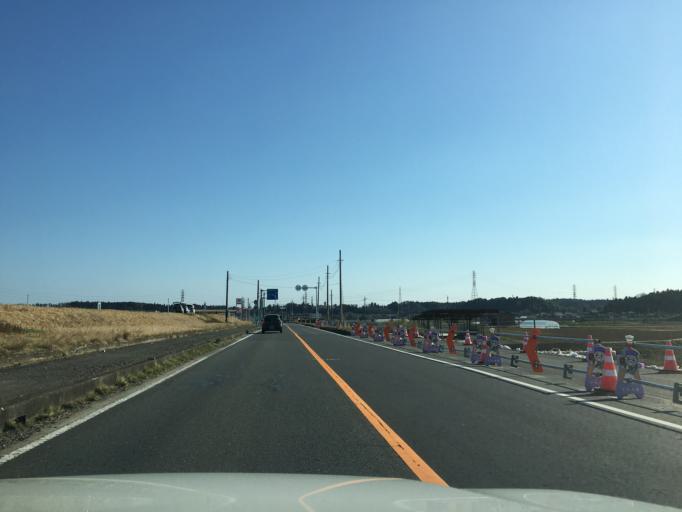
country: JP
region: Ibaraki
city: Mito-shi
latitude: 36.4262
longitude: 140.4216
